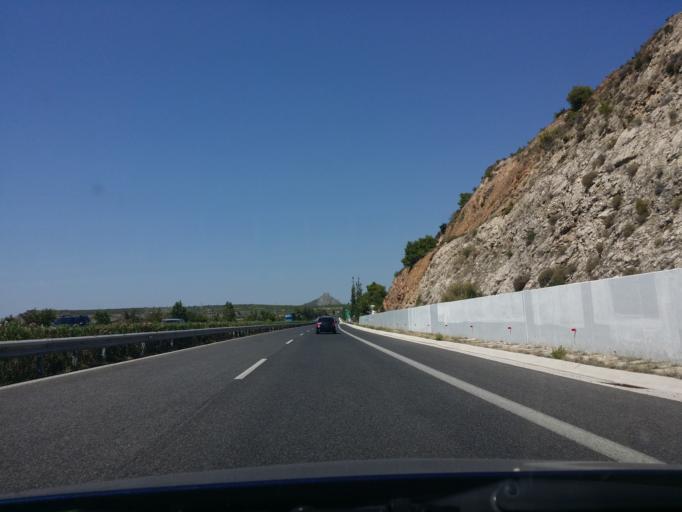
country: GR
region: Peloponnese
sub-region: Nomos Korinthias
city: Khiliomodhi
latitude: 37.8541
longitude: 22.8316
